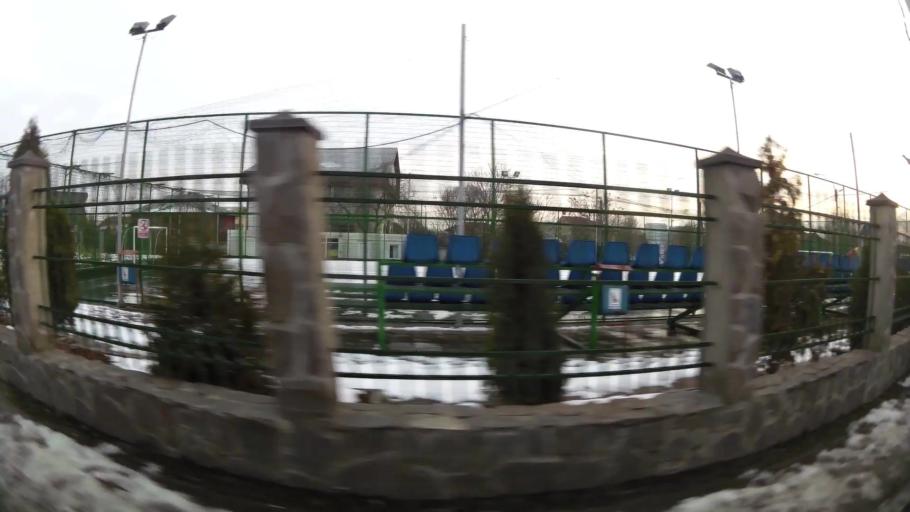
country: RO
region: Ilfov
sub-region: Comuna Fundeni-Dobroesti
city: Fundeni
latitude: 44.4563
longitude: 26.1708
